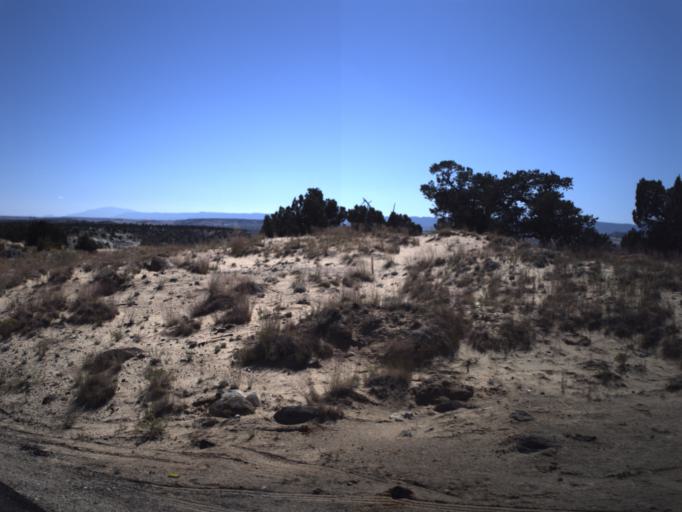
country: US
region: Utah
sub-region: Wayne County
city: Loa
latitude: 37.8359
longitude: -111.4186
